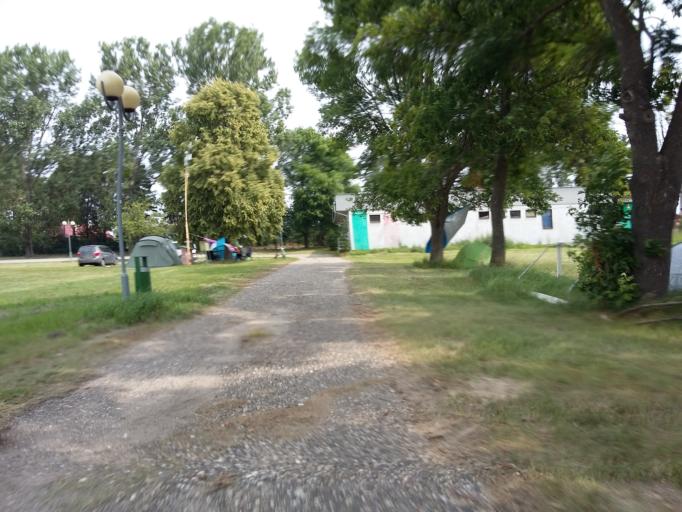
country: AT
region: Lower Austria
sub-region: Politischer Bezirk Ganserndorf
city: Drosing
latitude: 48.4902
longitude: 16.9566
